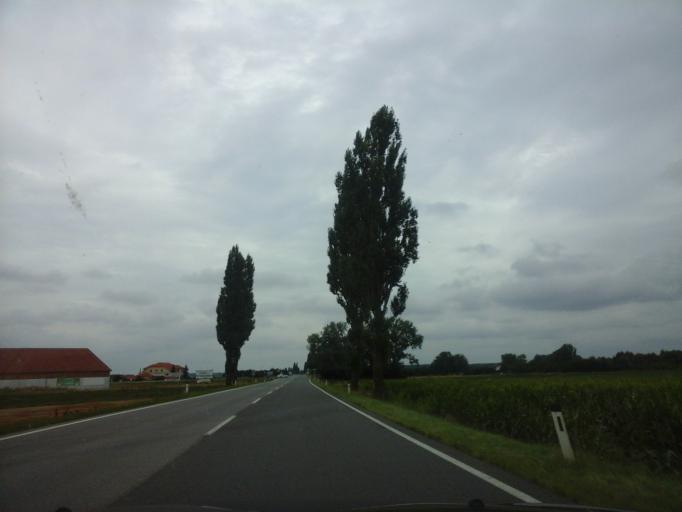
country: AT
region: Lower Austria
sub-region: Politischer Bezirk Ganserndorf
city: Engelhartstetten
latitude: 48.1816
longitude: 16.8925
